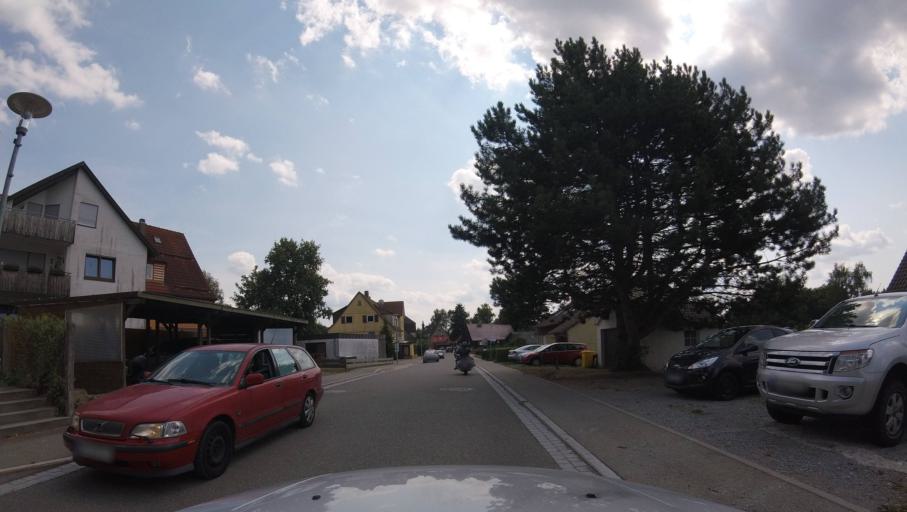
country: DE
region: Baden-Wuerttemberg
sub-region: Regierungsbezirk Stuttgart
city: Althutte
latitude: 48.9240
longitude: 9.5970
